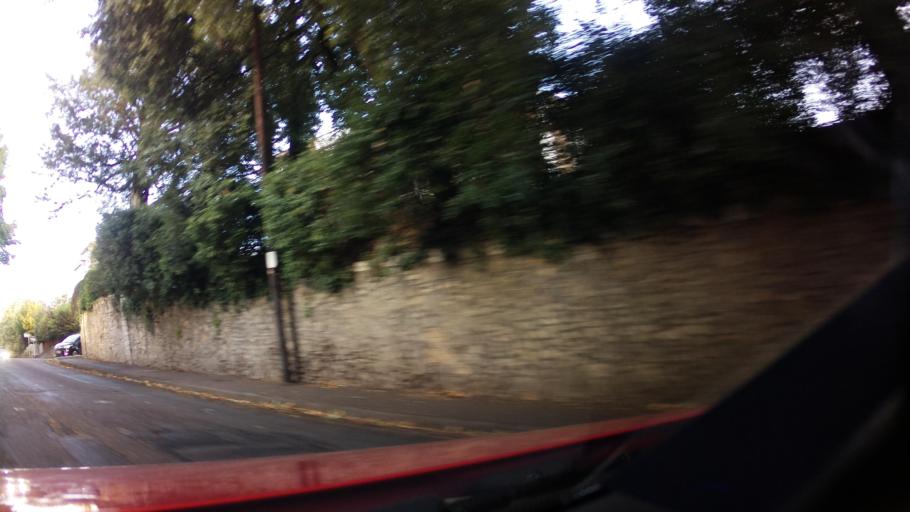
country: GB
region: England
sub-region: Bristol
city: Bristol
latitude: 51.4991
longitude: -2.6237
